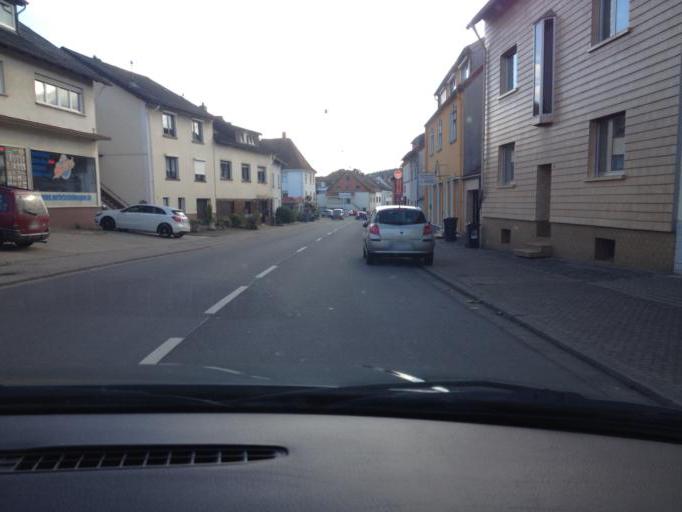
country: DE
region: Saarland
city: Marpingen
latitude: 49.4490
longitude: 7.0563
